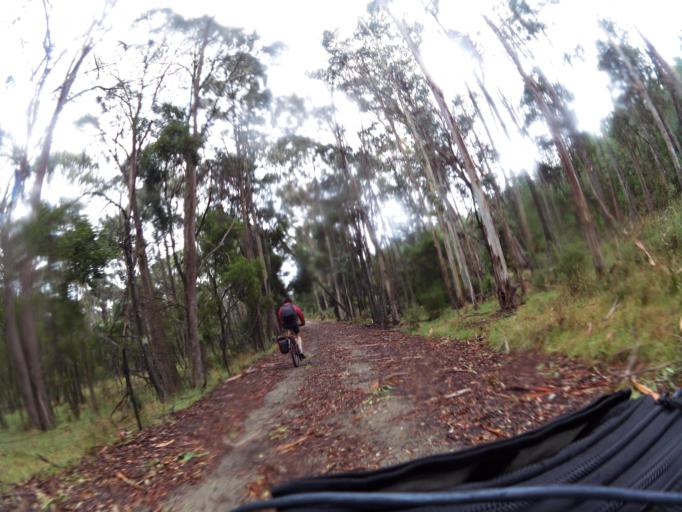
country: AU
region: New South Wales
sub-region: Greater Hume Shire
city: Holbrook
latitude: -36.1814
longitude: 147.5014
